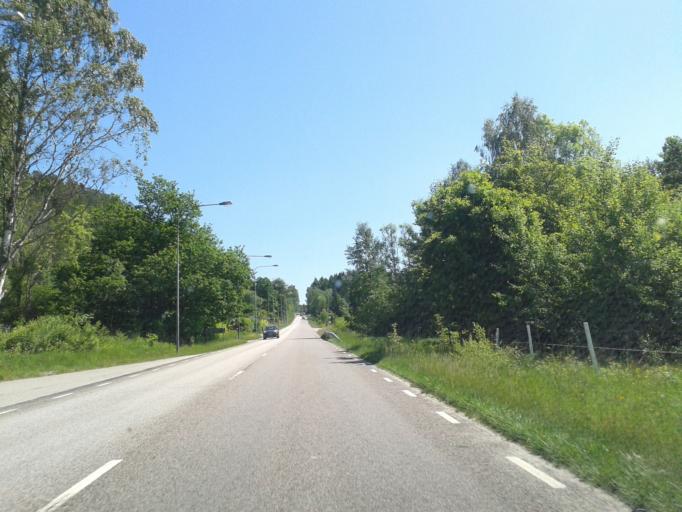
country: SE
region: Vaestra Goetaland
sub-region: Uddevalla Kommun
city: Uddevalla
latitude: 58.3289
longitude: 11.9206
